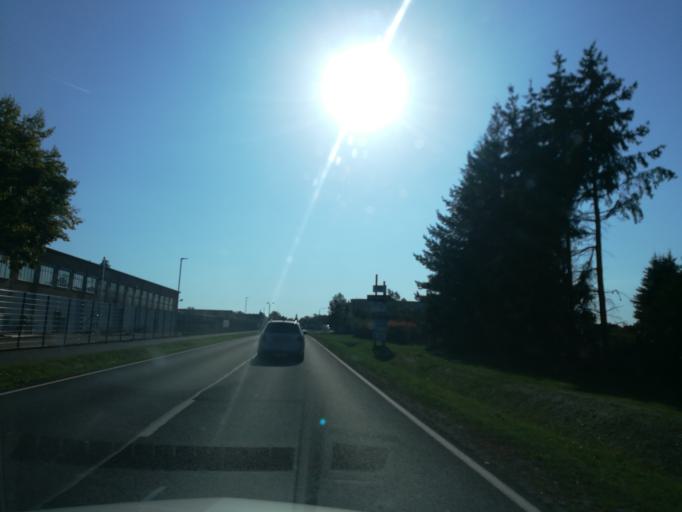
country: DE
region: Saxony-Anhalt
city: Gommern
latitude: 52.0795
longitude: 11.8185
